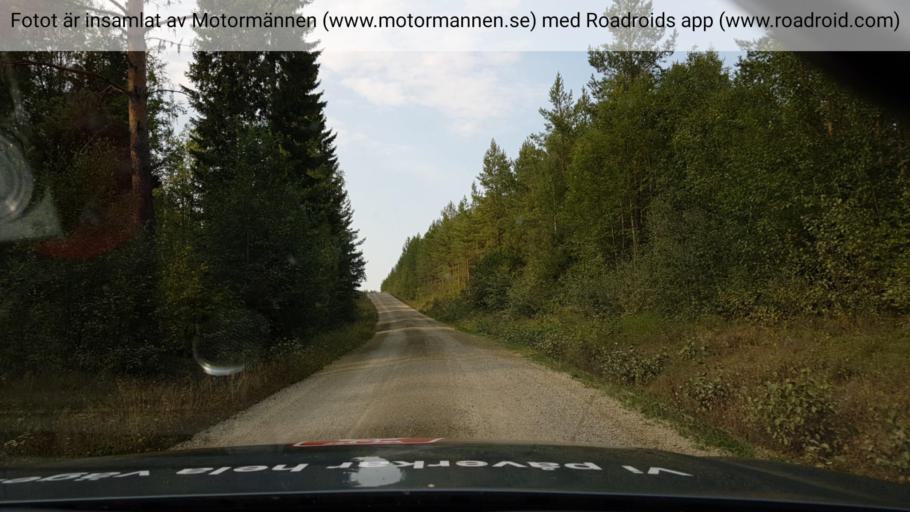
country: SE
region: Jaemtland
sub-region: Braecke Kommun
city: Braecke
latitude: 62.4657
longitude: 14.9187
